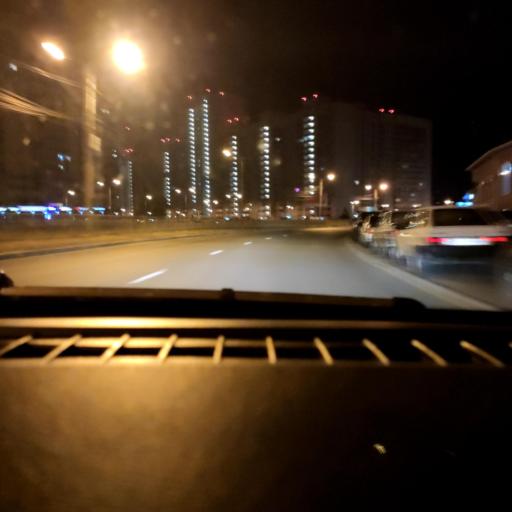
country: RU
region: Voronezj
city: Voronezh
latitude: 51.7133
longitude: 39.1929
